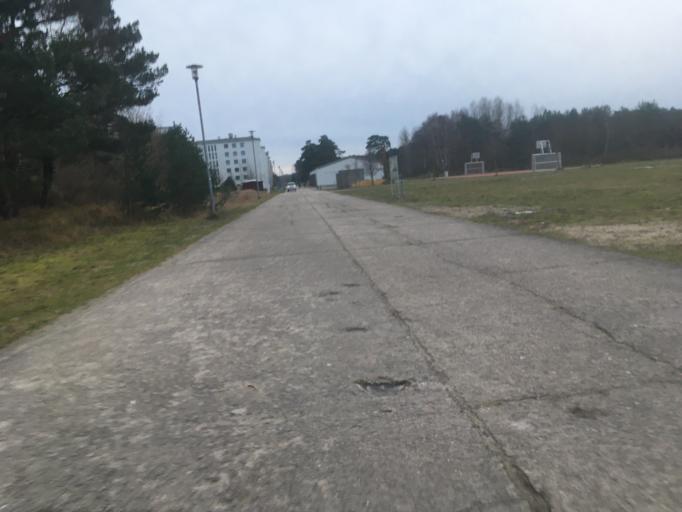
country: DE
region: Mecklenburg-Vorpommern
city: Ostseebad Binz
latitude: 54.4532
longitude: 13.5686
